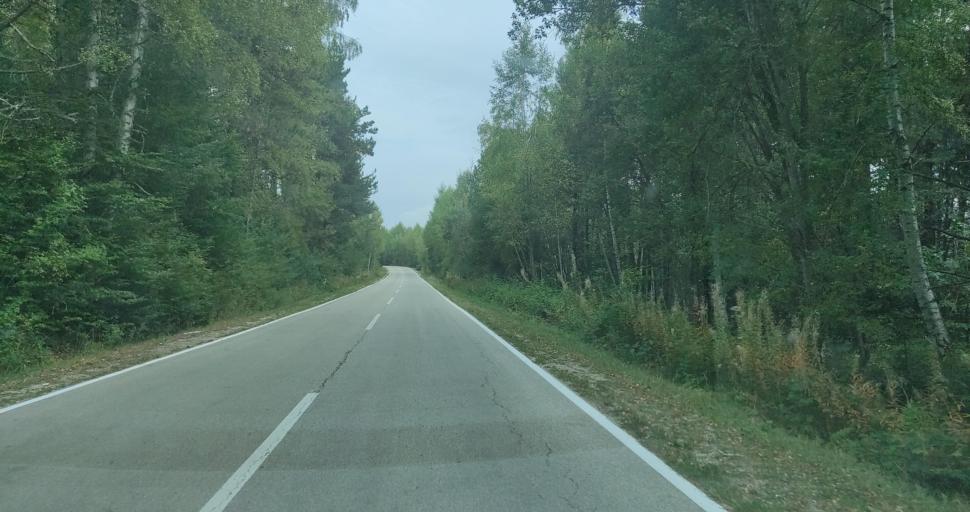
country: RS
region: Central Serbia
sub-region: Jablanicki Okrug
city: Crna Trava
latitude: 42.7260
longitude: 22.3361
